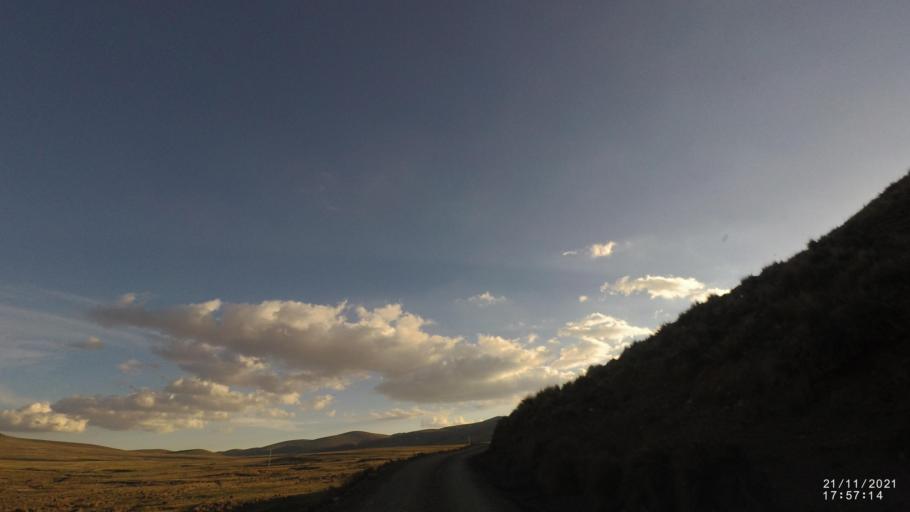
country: BO
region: Cochabamba
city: Cochabamba
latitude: -17.2269
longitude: -66.2320
